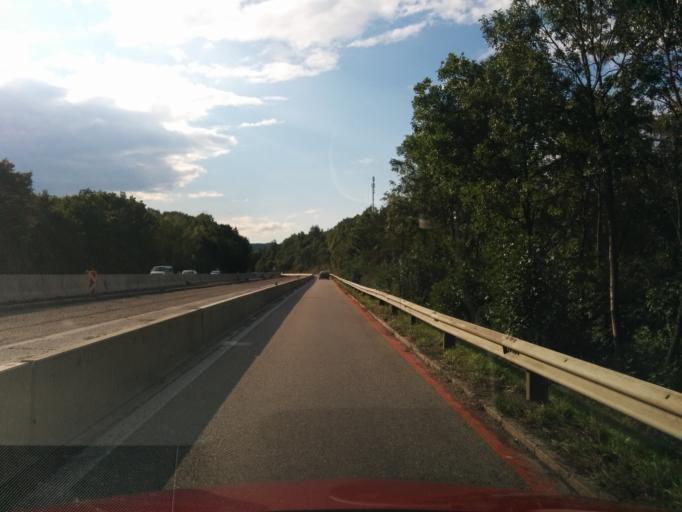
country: AT
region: Lower Austria
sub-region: Politischer Bezirk Wien-Umgebung
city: Pressbaum
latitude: 48.1772
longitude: 16.0965
